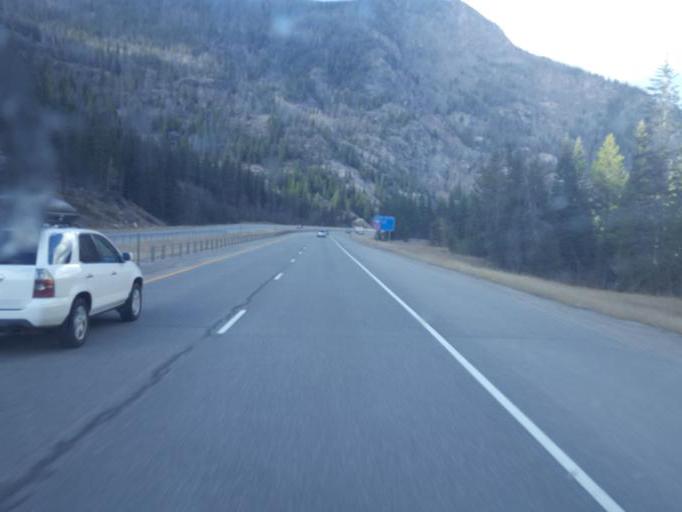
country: US
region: Colorado
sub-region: Summit County
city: Frisco
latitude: 39.5585
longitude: -106.1300
